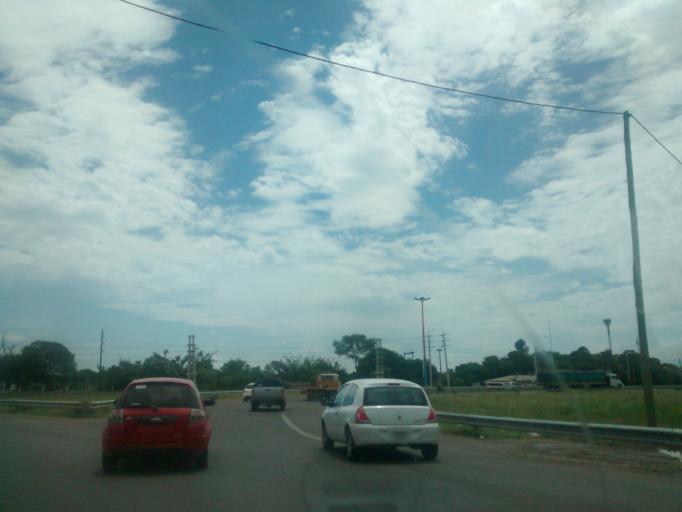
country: AR
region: Chaco
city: Fontana
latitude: -27.4113
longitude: -59.0021
